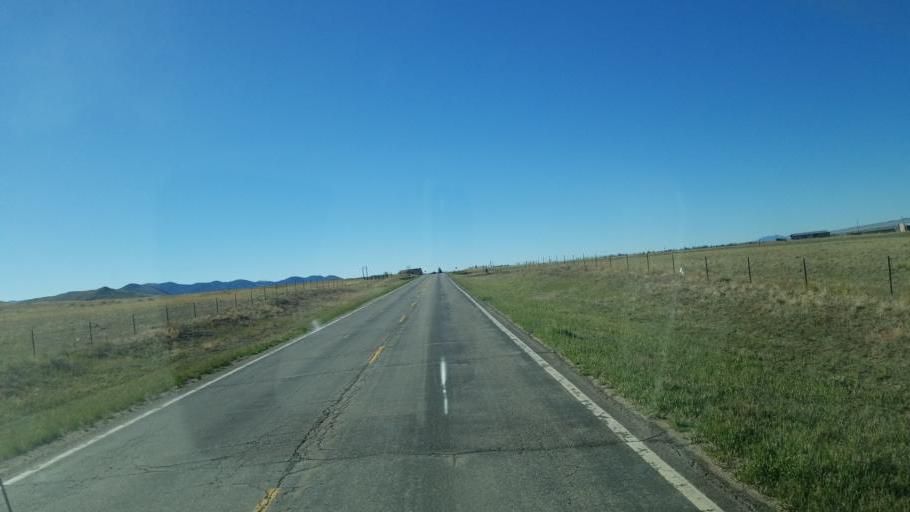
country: US
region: Colorado
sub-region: Custer County
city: Westcliffe
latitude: 38.1661
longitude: -105.4874
